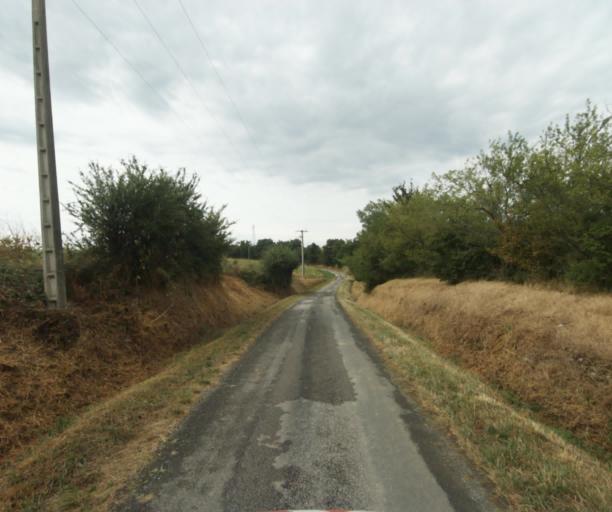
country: FR
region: Midi-Pyrenees
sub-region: Departement de la Haute-Garonne
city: Revel
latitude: 43.4337
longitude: 1.9679
